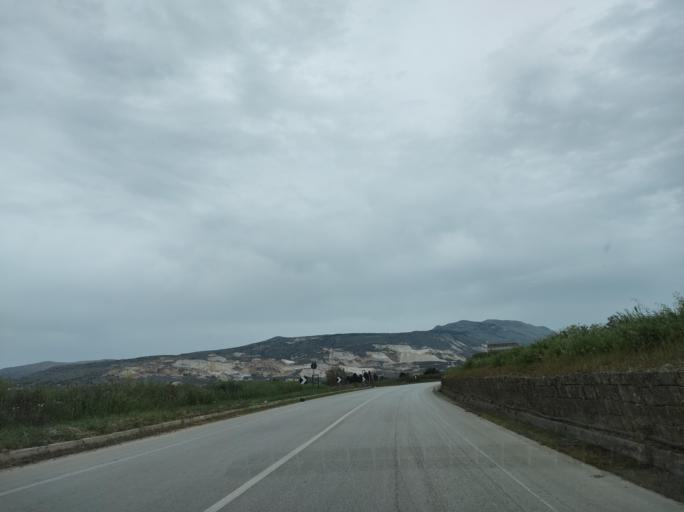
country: IT
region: Sicily
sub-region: Trapani
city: Custonaci
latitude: 38.0409
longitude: 12.6692
